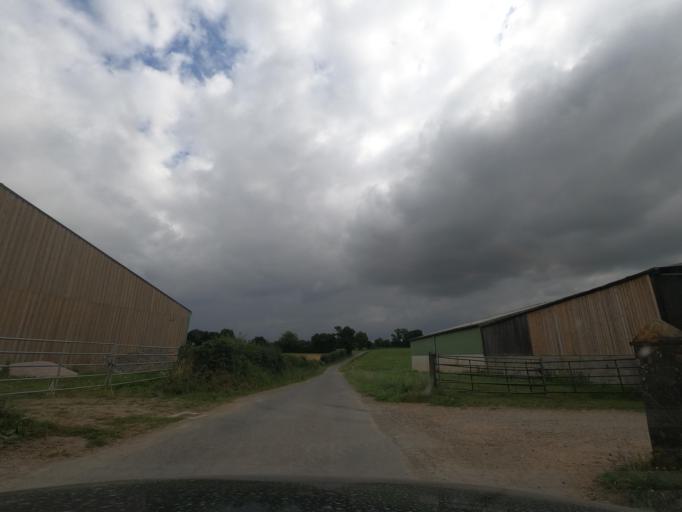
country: FR
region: Lower Normandy
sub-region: Departement de l'Orne
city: Briouze
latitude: 48.7238
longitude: -0.3245
